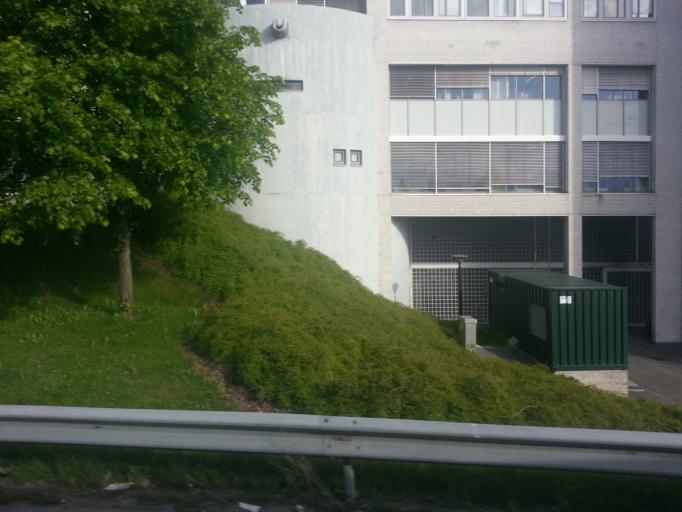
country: NO
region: Akershus
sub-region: Baerum
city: Sandvika
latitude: 59.8886
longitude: 10.5246
